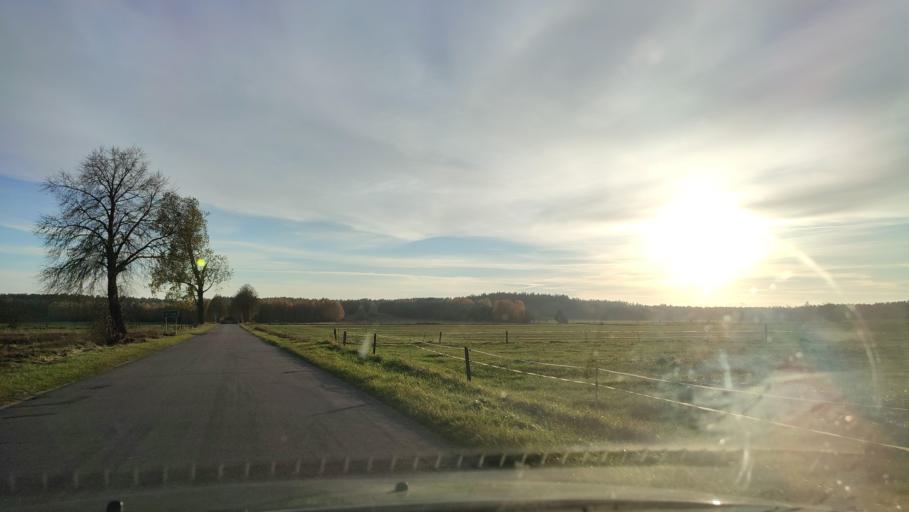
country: PL
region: Masovian Voivodeship
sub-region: Powiat mlawski
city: Dzierzgowo
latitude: 53.3080
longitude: 20.6697
